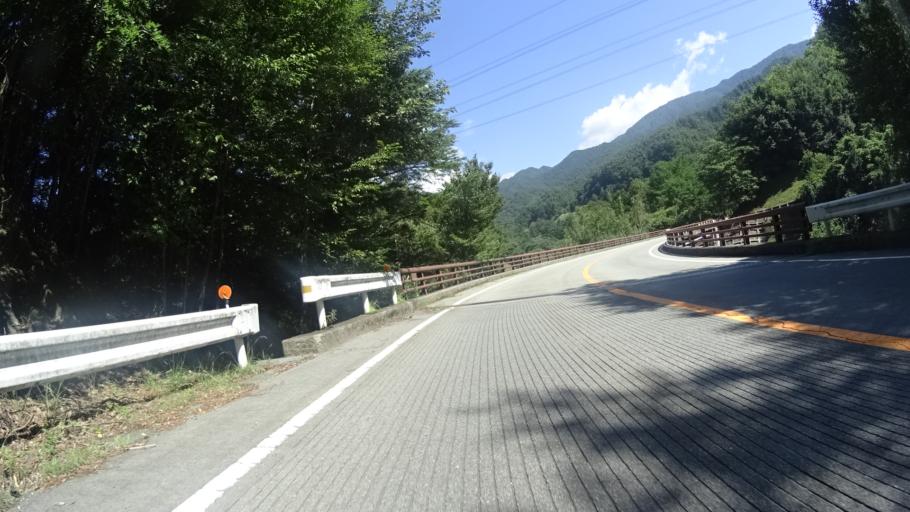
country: JP
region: Yamanashi
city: Enzan
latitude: 35.7414
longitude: 138.8074
